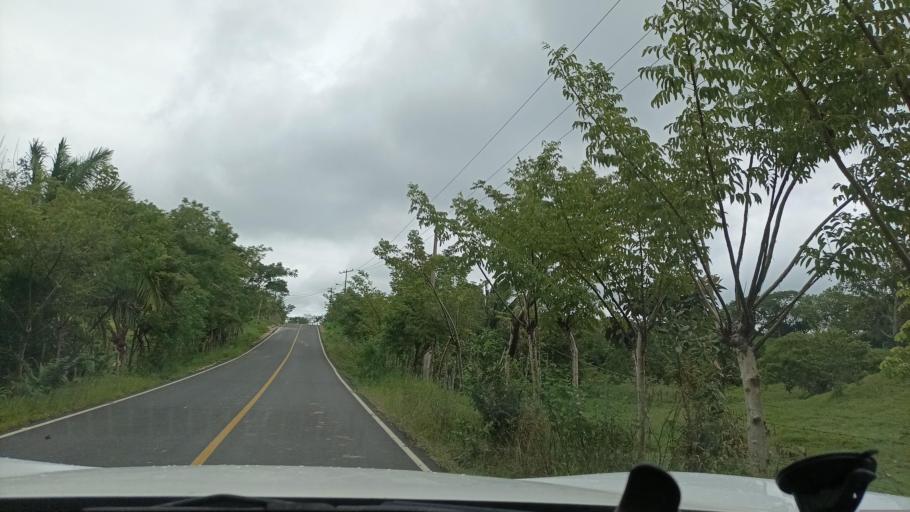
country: MX
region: Veracruz
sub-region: Moloacan
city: Cuichapa
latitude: 17.8072
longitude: -94.3561
